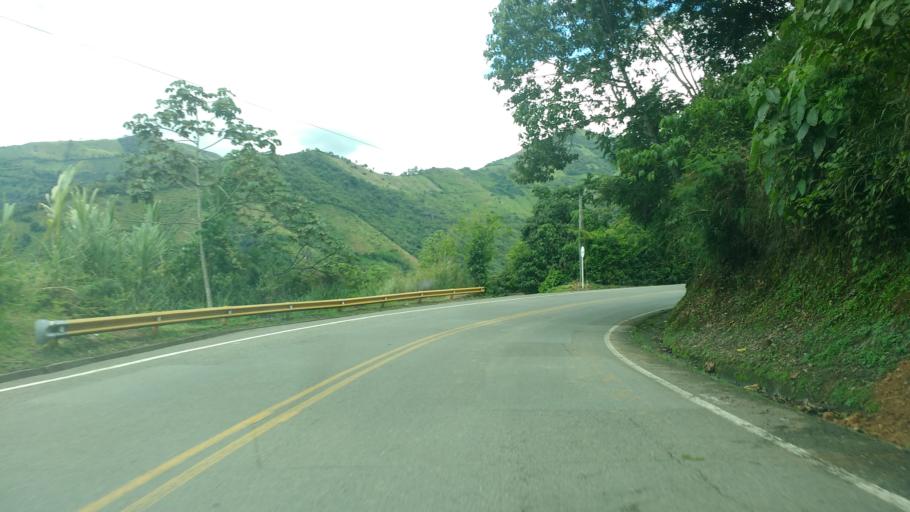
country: CO
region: Antioquia
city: Amaga
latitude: 6.0613
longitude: -75.7457
